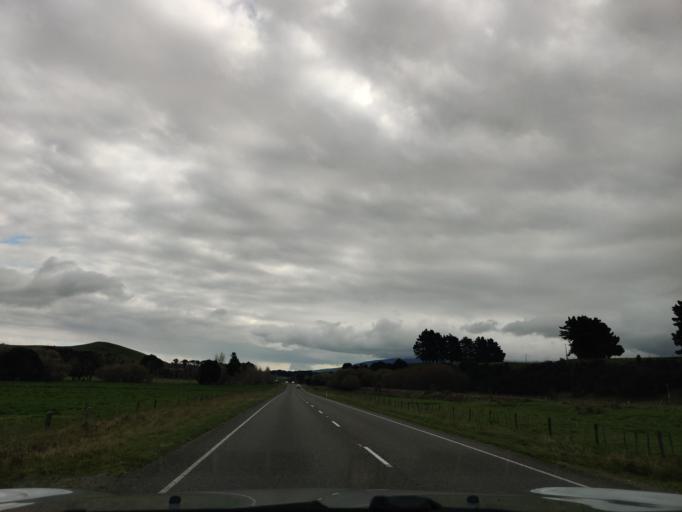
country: NZ
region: Manawatu-Wanganui
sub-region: Palmerston North City
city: Palmerston North
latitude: -40.2817
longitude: 175.9935
